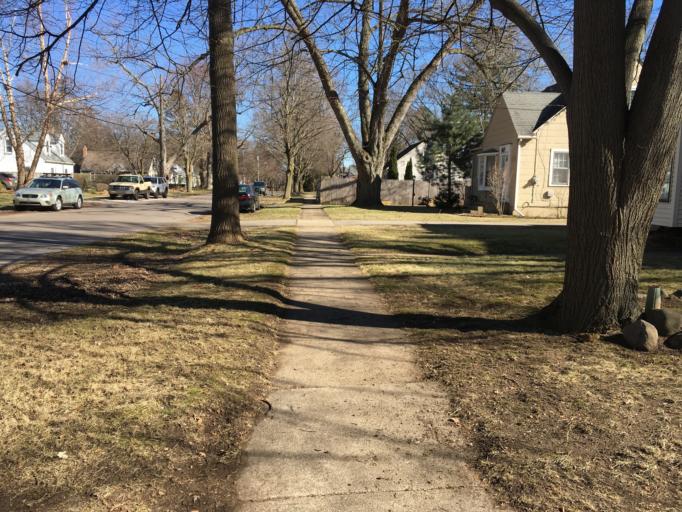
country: US
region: Michigan
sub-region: Kalamazoo County
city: Westwood
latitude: 42.2628
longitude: -85.6249
